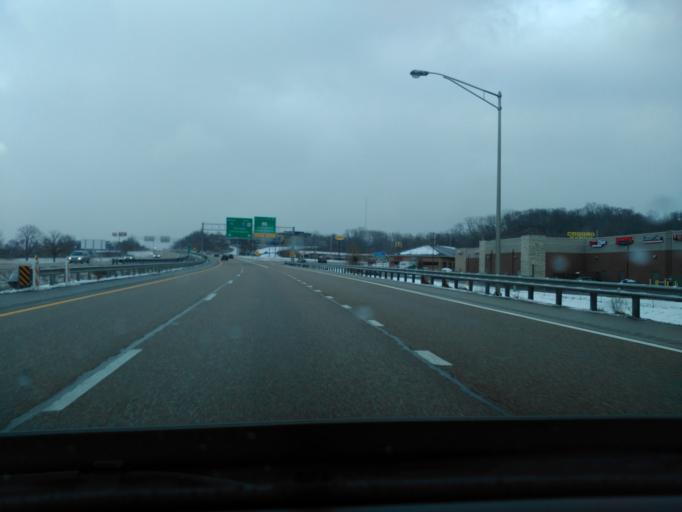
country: US
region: Illinois
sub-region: Madison County
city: Collinsville
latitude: 38.6775
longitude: -90.0157
